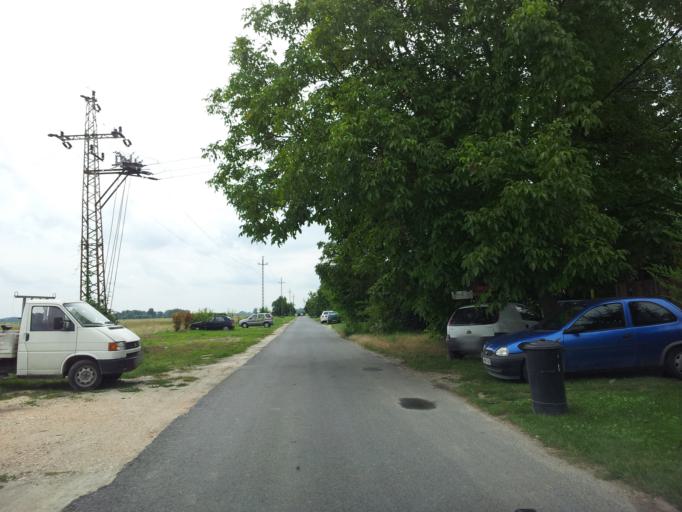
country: HU
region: Pest
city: Rackeve
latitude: 47.1925
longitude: 18.9604
